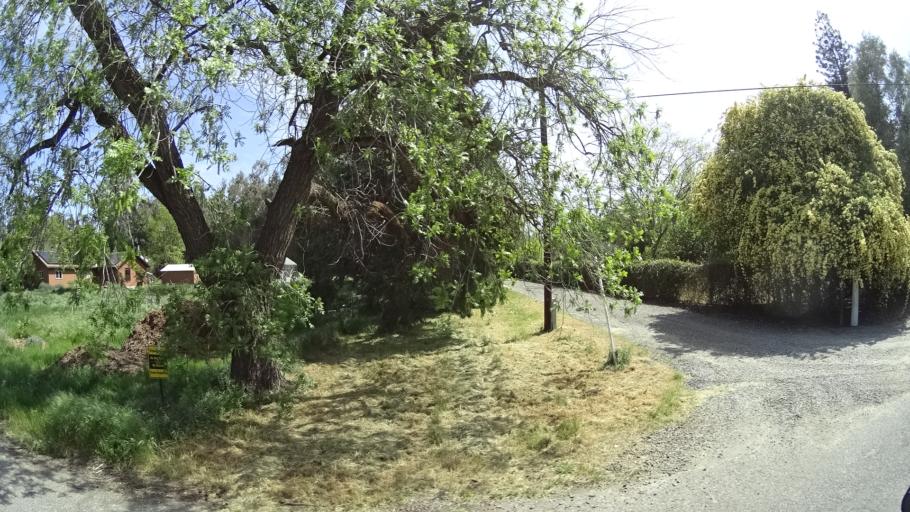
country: US
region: California
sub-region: Glenn County
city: Hamilton City
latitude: 39.8025
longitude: -122.0570
